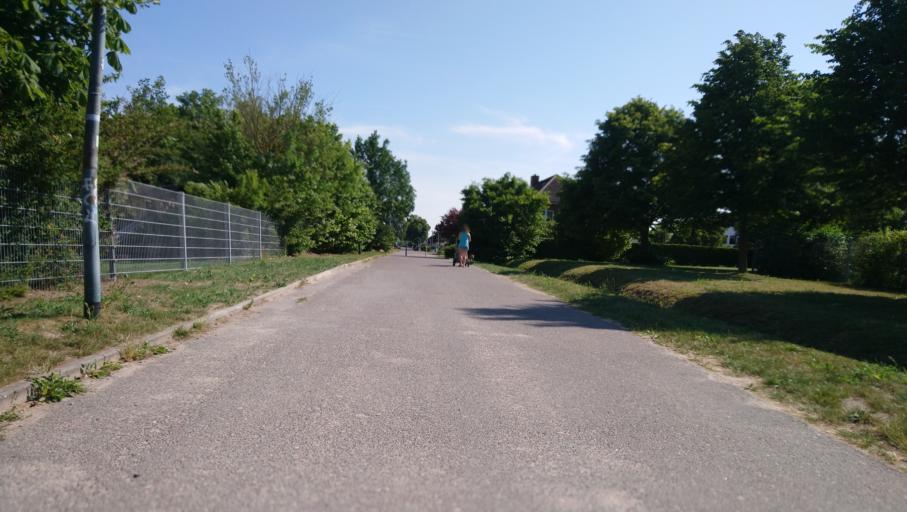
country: DE
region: Mecklenburg-Vorpommern
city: Roggentin
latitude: 54.0846
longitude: 12.1862
